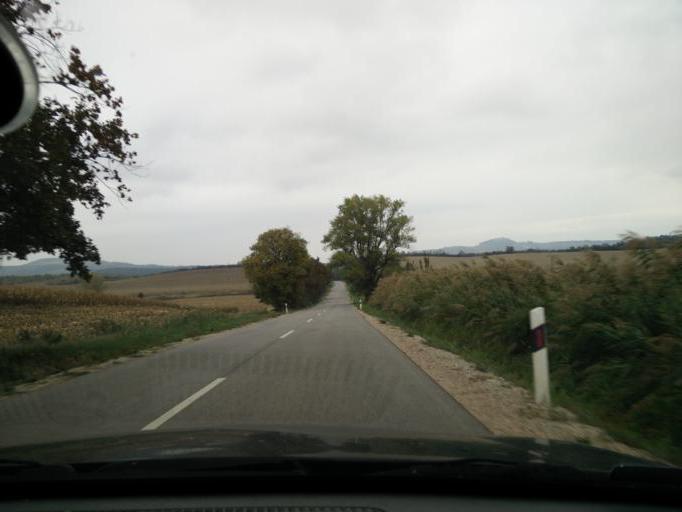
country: HU
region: Komarom-Esztergom
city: Bajna
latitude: 47.6882
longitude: 18.6095
